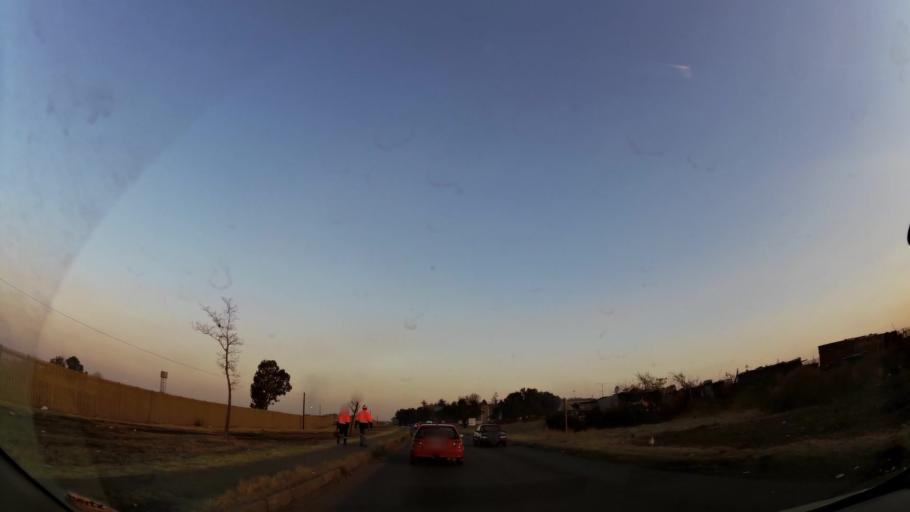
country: ZA
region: Gauteng
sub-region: Ekurhuleni Metropolitan Municipality
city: Springs
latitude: -26.2863
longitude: 28.4046
